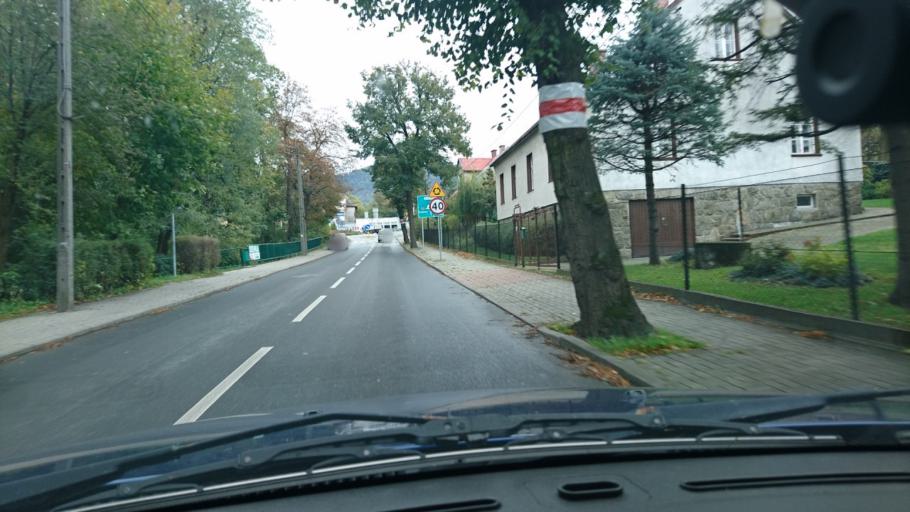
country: PL
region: Silesian Voivodeship
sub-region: Powiat bielski
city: Kozy
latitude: 49.8455
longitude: 19.1414
